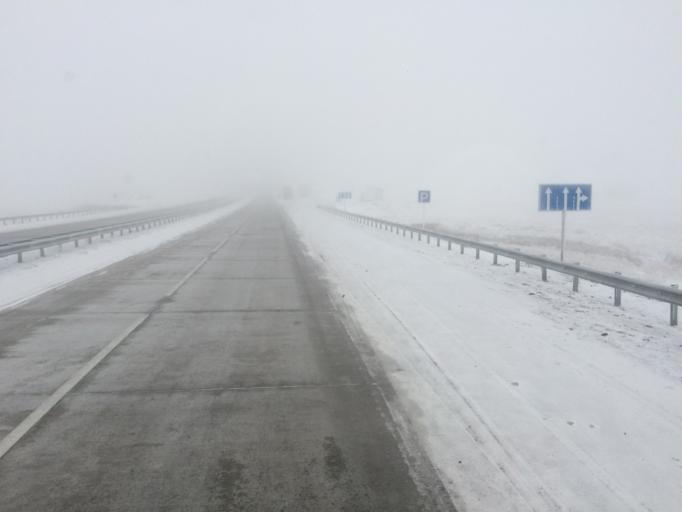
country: KZ
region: Zhambyl
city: Georgiyevka
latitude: 43.4324
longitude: 74.9381
